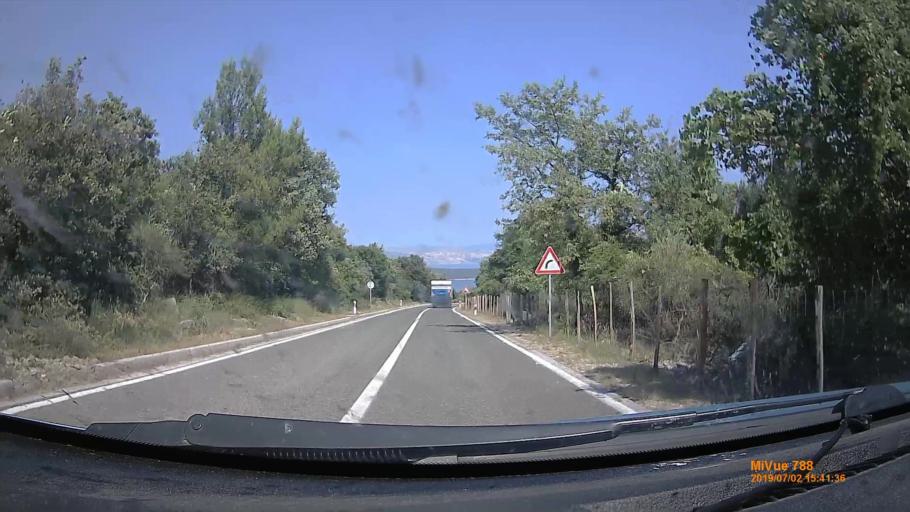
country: HR
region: Primorsko-Goranska
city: Cres
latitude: 44.9610
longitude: 14.4446
